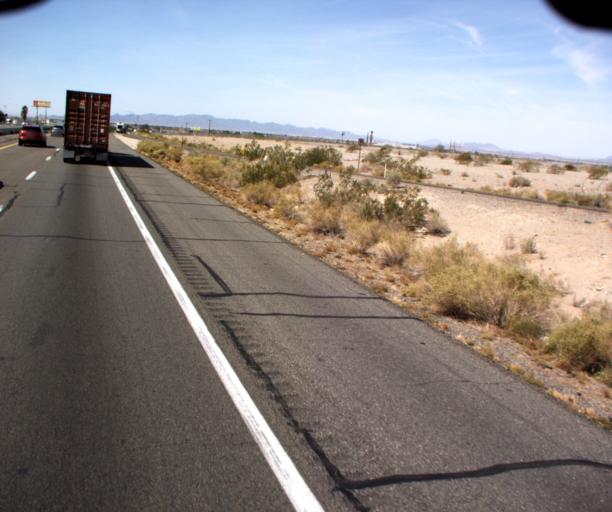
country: US
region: Arizona
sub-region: La Paz County
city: Ehrenberg
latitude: 33.6027
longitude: -114.5202
